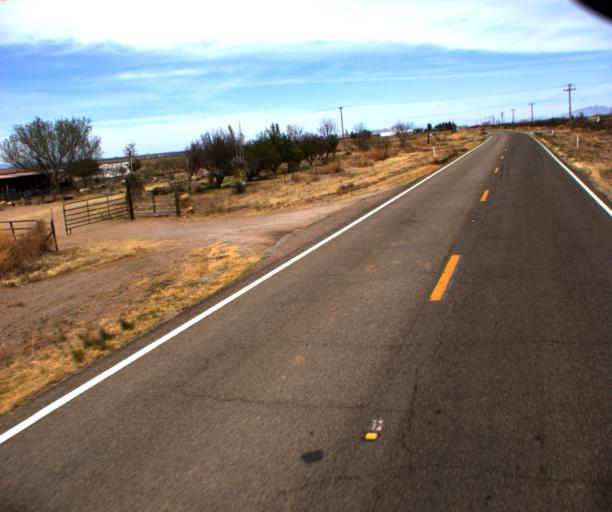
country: US
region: Arizona
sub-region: Cochise County
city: Bisbee
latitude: 31.7281
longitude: -109.6870
